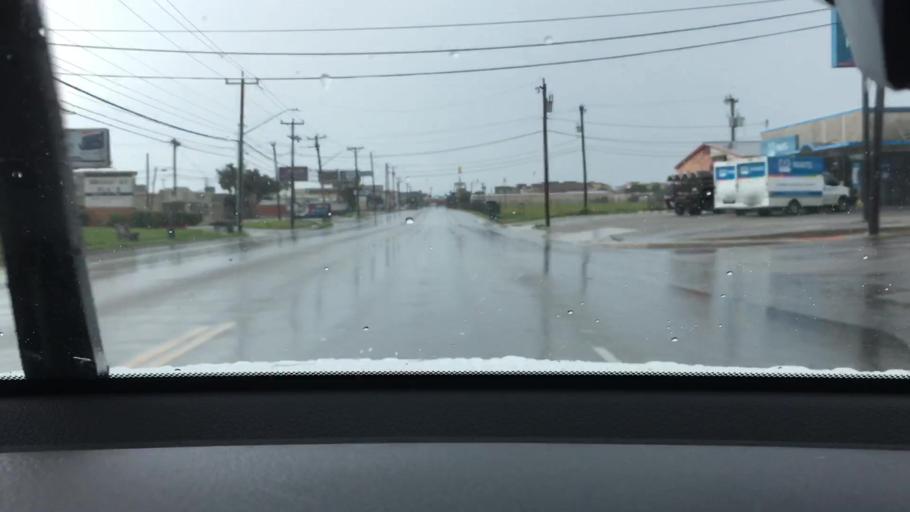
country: US
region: Texas
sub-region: Bexar County
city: Alamo Heights
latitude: 29.5239
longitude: -98.4575
